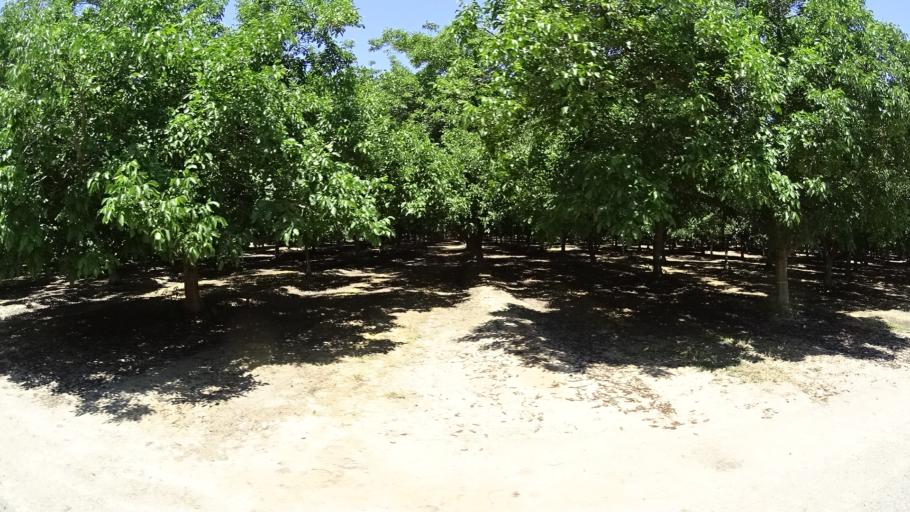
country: US
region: California
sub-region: Kings County
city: Lucerne
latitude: 36.4303
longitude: -119.5977
